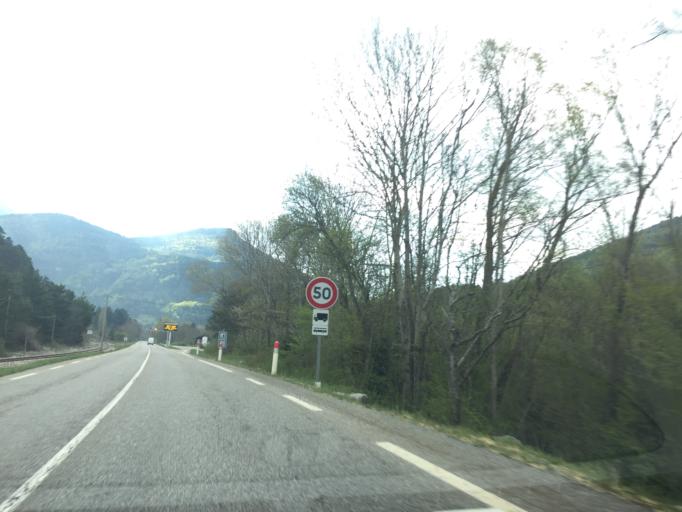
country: FR
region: Provence-Alpes-Cote d'Azur
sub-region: Departement des Hautes-Alpes
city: Veynes
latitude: 44.6210
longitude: 5.7002
